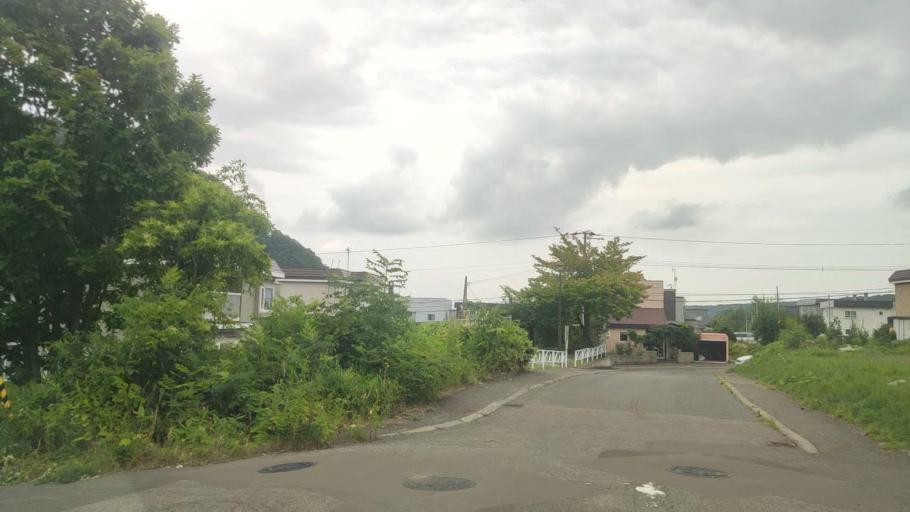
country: JP
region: Hokkaido
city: Sapporo
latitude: 42.9642
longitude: 141.3171
